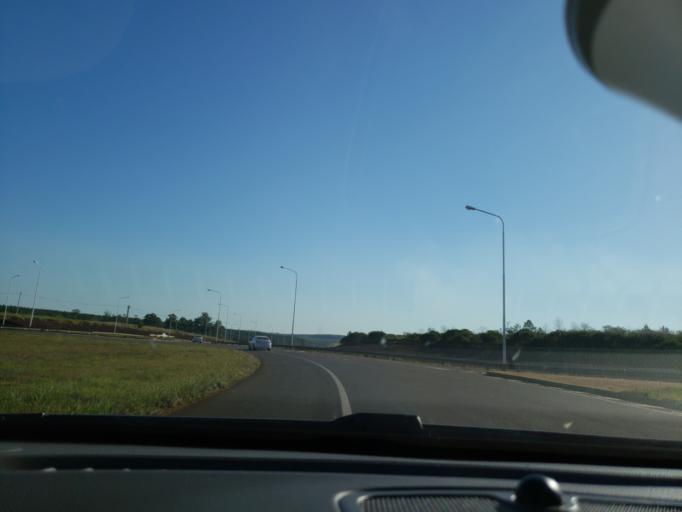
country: AR
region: Misiones
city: Garupa
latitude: -27.4651
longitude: -55.9188
